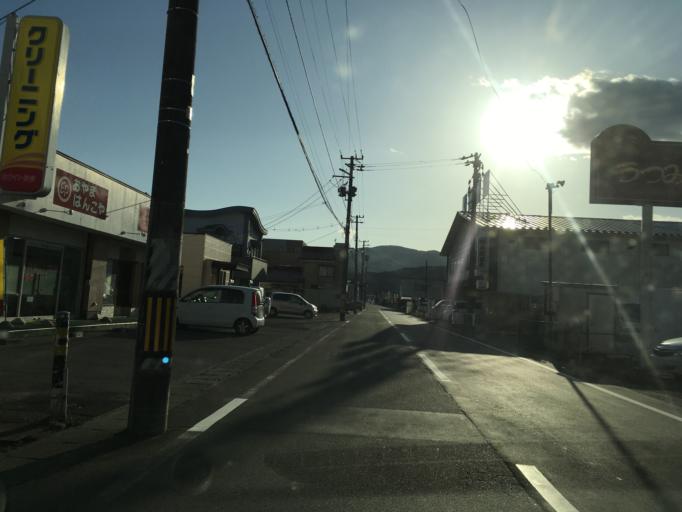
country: JP
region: Iwate
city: Ofunato
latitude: 38.8933
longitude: 141.5657
